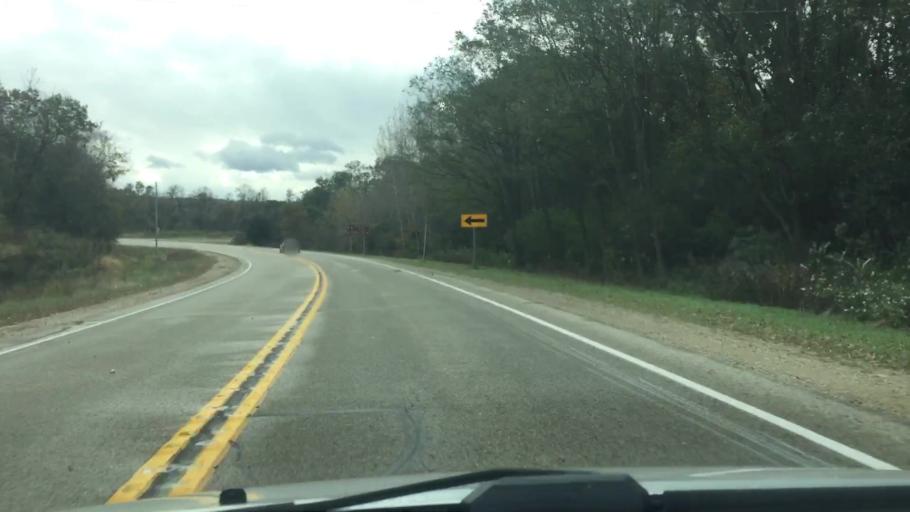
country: US
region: Wisconsin
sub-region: Waukesha County
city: Eagle
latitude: 42.9398
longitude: -88.4743
